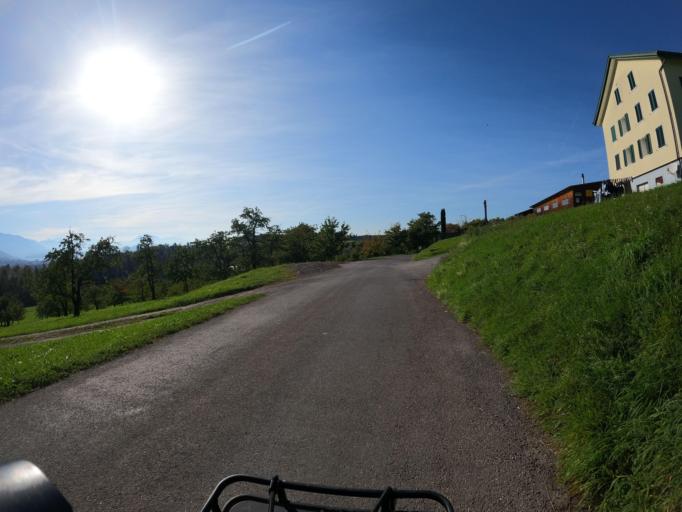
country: CH
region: Zug
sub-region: Zug
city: Baar
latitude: 47.2180
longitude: 8.5408
